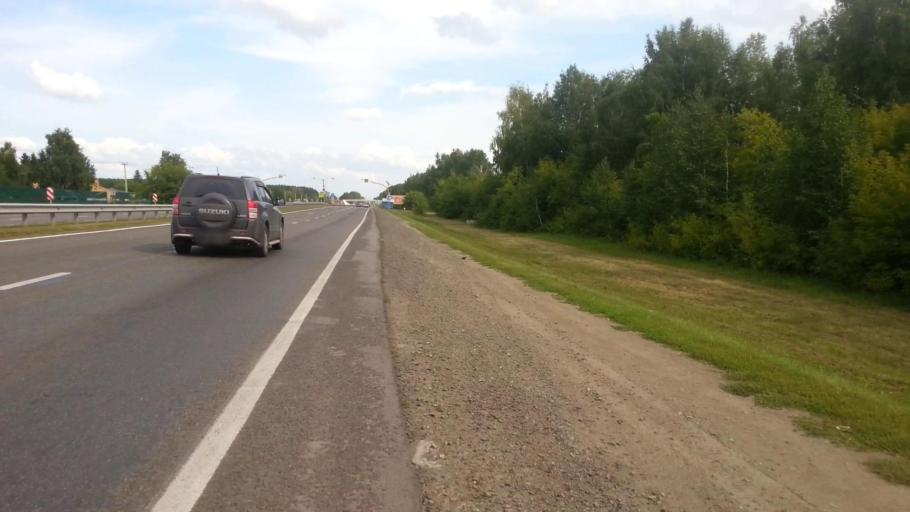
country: RU
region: Altai Krai
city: Vlasikha
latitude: 53.3546
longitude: 83.5380
